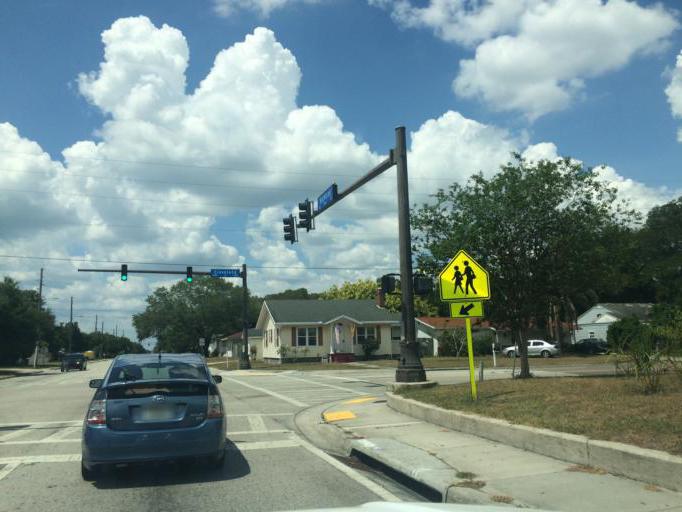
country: US
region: Florida
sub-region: Pinellas County
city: Clearwater
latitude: 27.9653
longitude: -82.7753
